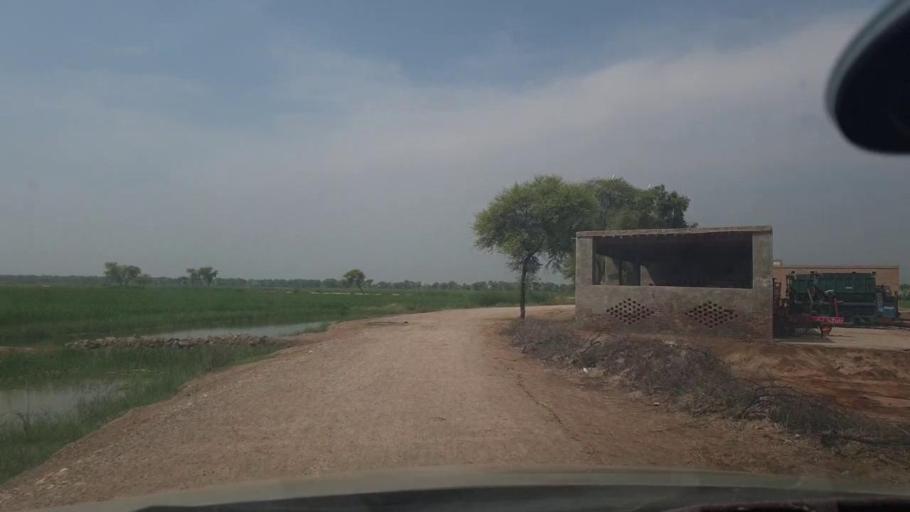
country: PK
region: Sindh
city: Jacobabad
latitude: 28.2691
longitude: 68.5125
